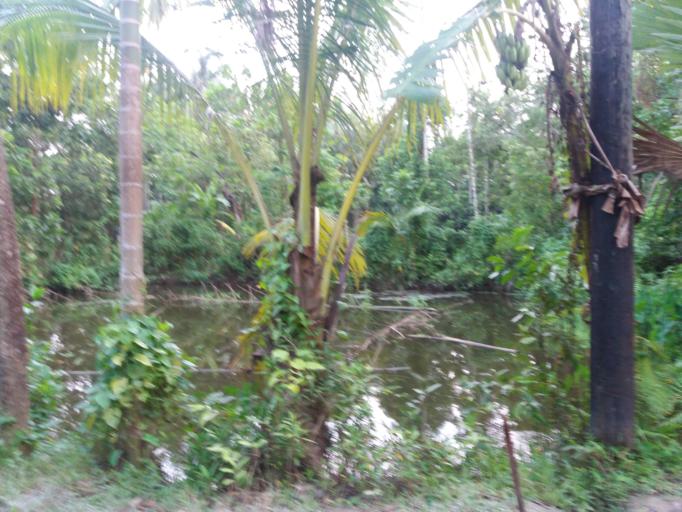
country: BD
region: Chittagong
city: Feni
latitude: 22.9339
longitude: 91.3484
